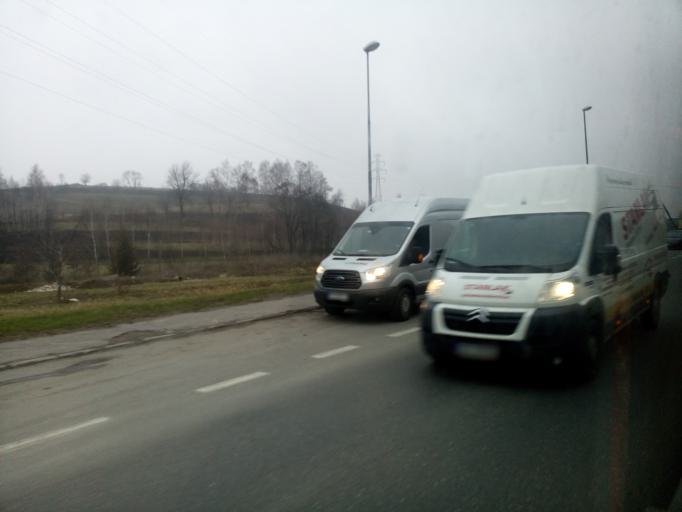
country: PL
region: Lesser Poland Voivodeship
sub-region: Powiat nowosadecki
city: Stary Sacz
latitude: 49.5759
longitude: 20.6635
